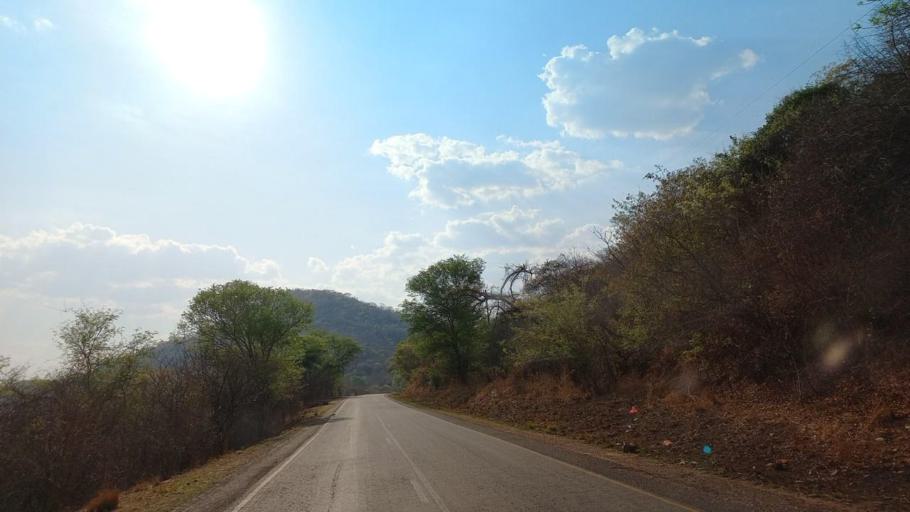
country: ZM
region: Lusaka
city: Luangwa
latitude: -14.9855
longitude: 30.1904
